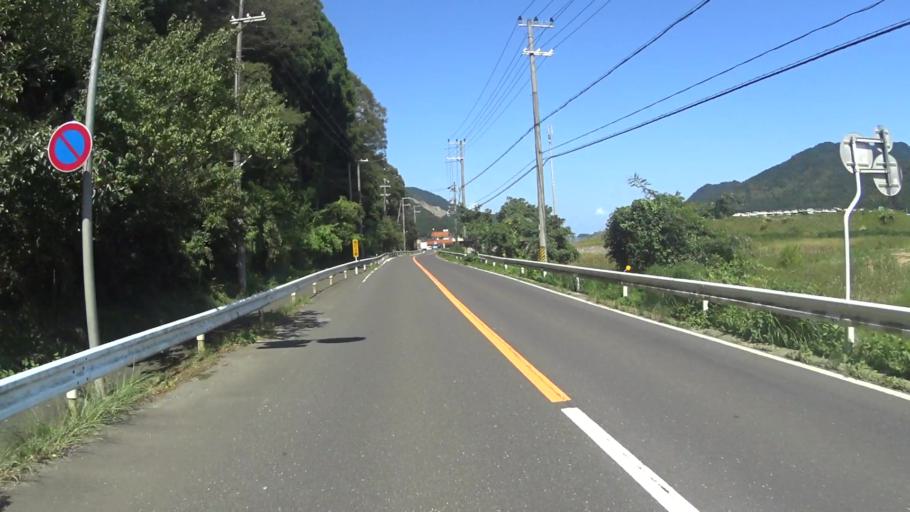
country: JP
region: Kyoto
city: Maizuru
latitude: 35.4683
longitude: 135.2779
